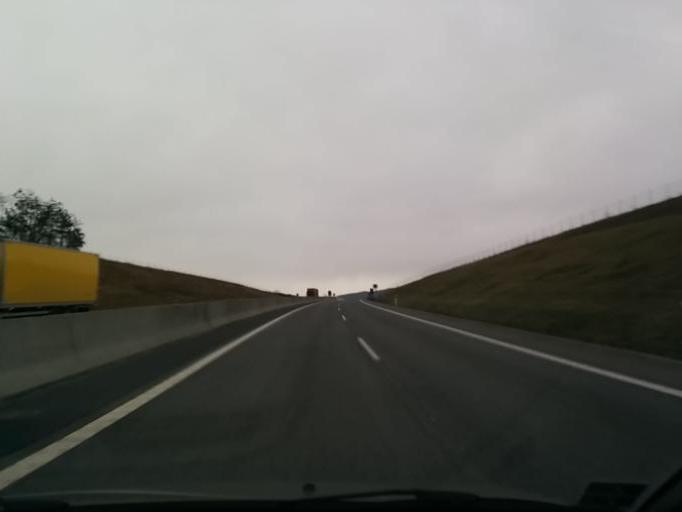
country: SK
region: Nitriansky
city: Tlmace
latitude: 48.3727
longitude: 18.5174
